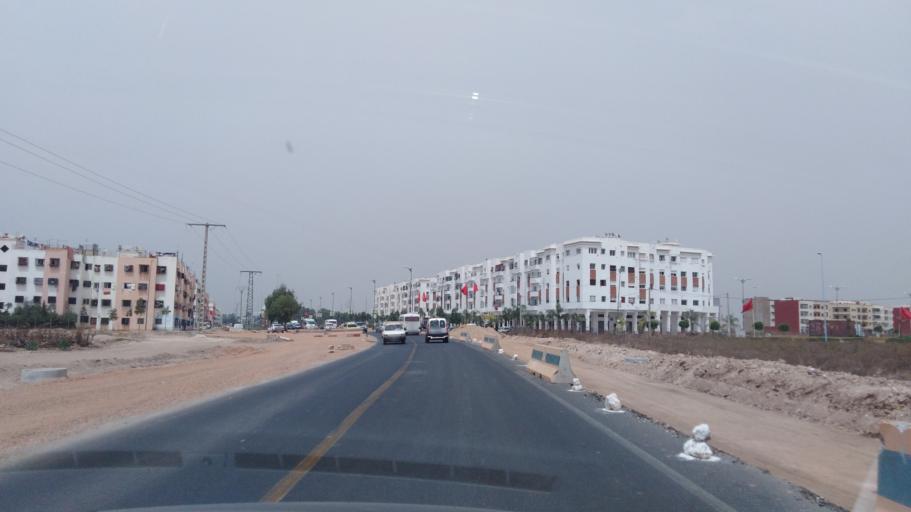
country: MA
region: Chaouia-Ouardigha
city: Nouaseur
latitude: 33.3611
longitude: -7.5466
